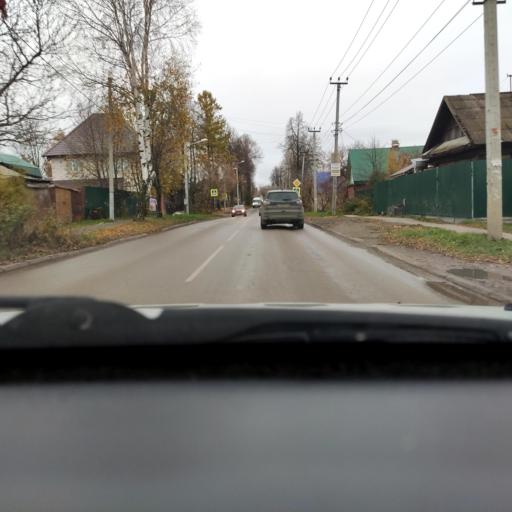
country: RU
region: Perm
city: Perm
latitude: 58.0229
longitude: 56.3364
